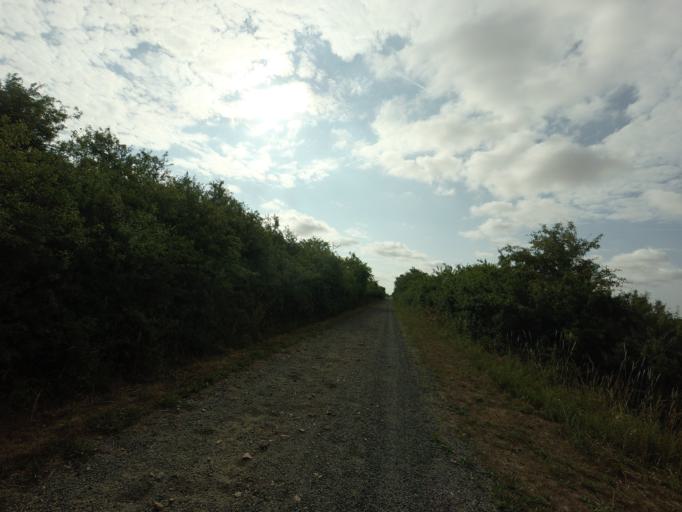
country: SE
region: Skane
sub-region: Helsingborg
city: Odakra
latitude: 56.1637
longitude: 12.7371
